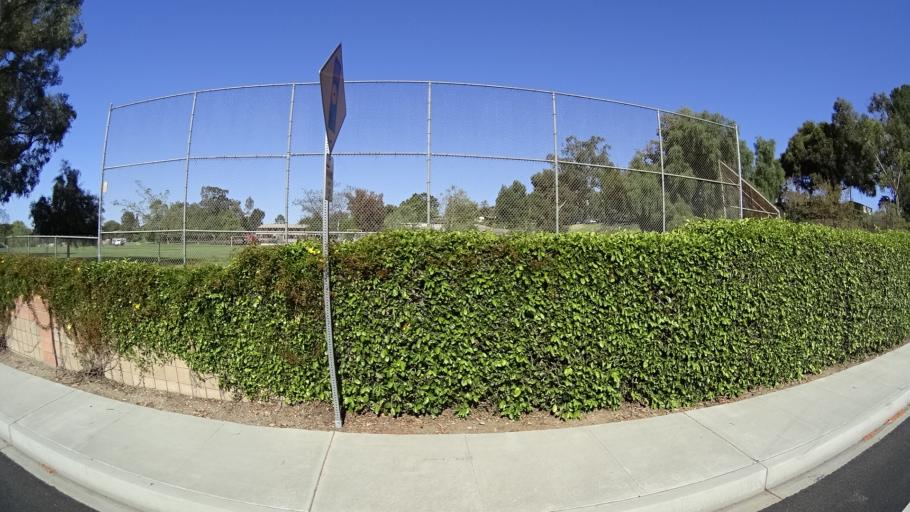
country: US
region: California
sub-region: Ventura County
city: Casa Conejo
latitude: 34.1974
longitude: -118.8904
